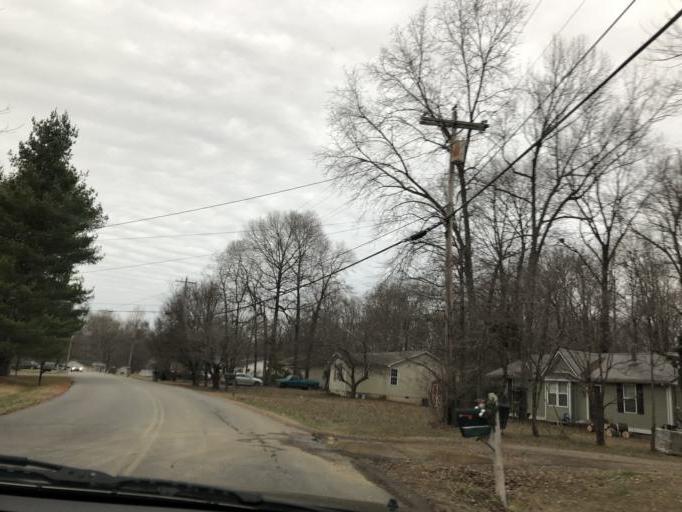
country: US
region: Tennessee
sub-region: Sumner County
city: White House
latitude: 36.4259
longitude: -86.6788
